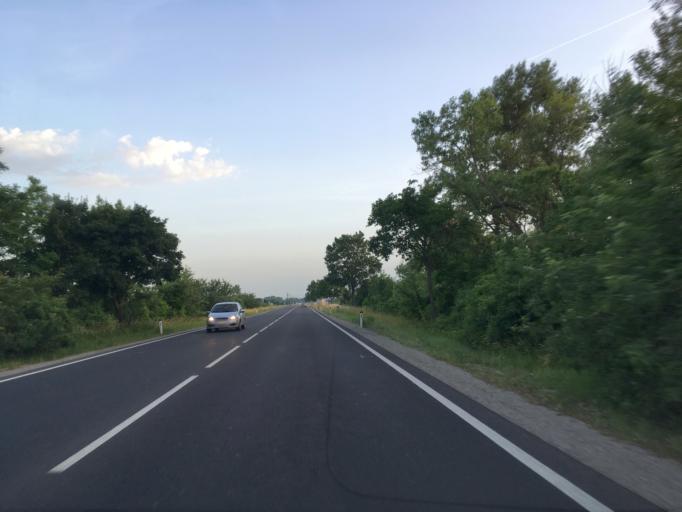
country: AT
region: Lower Austria
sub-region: Politischer Bezirk Baden
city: Teesdorf
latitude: 47.9640
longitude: 16.2735
